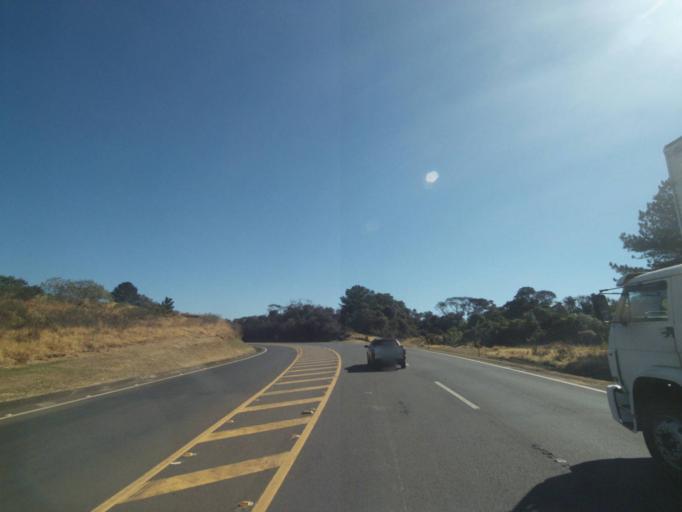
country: BR
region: Parana
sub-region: Tibagi
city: Tibagi
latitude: -24.7158
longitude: -50.5422
